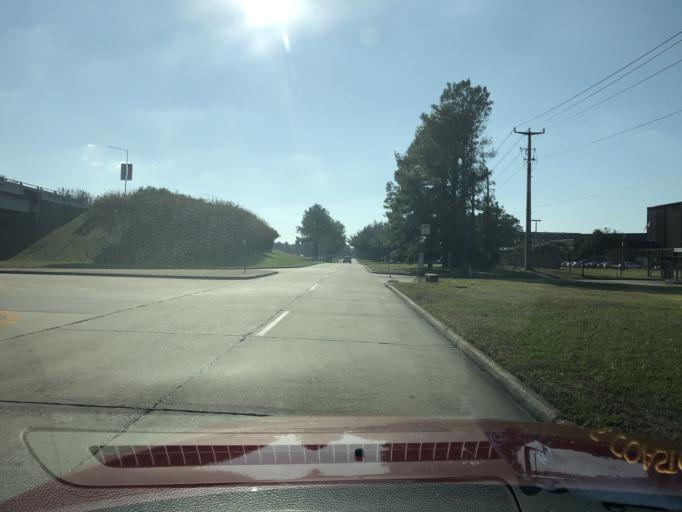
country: US
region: Texas
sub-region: Harris County
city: Aldine
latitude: 29.9653
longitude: -95.3367
